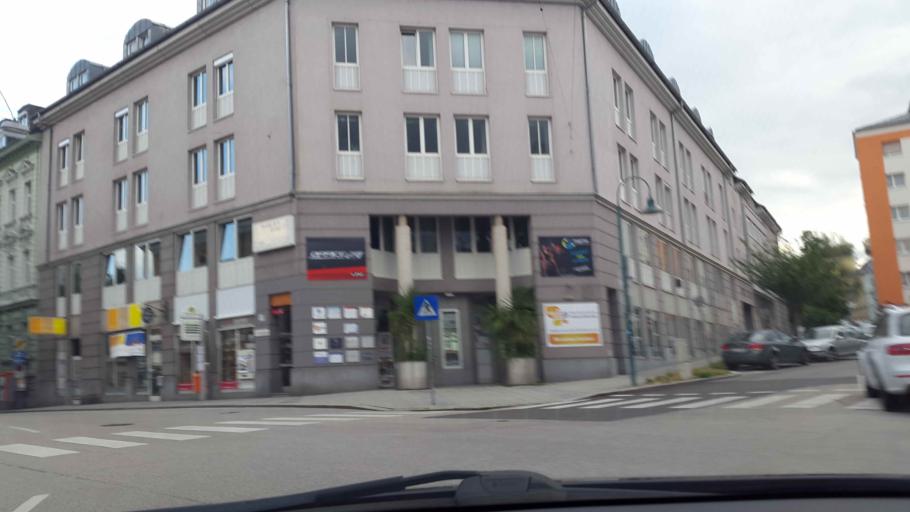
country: AT
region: Upper Austria
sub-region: Linz Stadt
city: Linz
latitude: 48.3155
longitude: 14.2804
